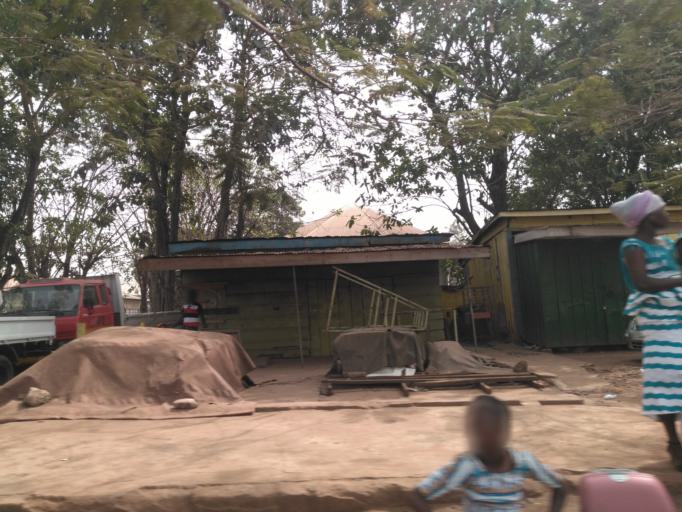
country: GH
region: Ashanti
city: Kumasi
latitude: 6.7106
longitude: -1.6296
